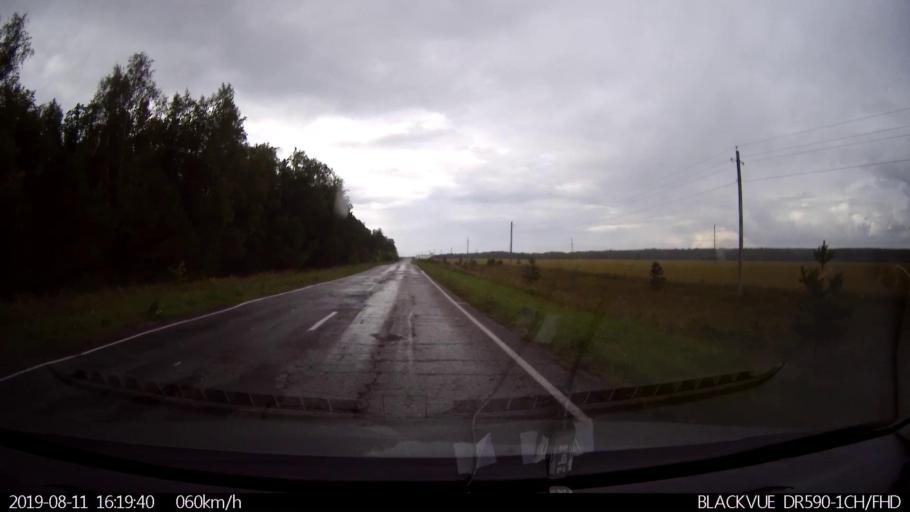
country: RU
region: Ulyanovsk
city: Mayna
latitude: 54.0656
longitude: 47.6063
